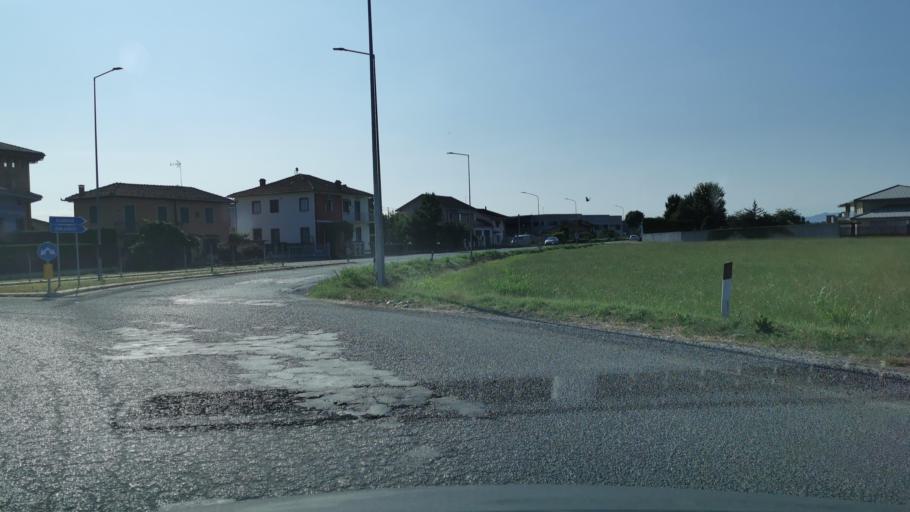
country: IT
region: Piedmont
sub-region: Provincia di Torino
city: Cavour
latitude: 44.7459
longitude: 7.4097
